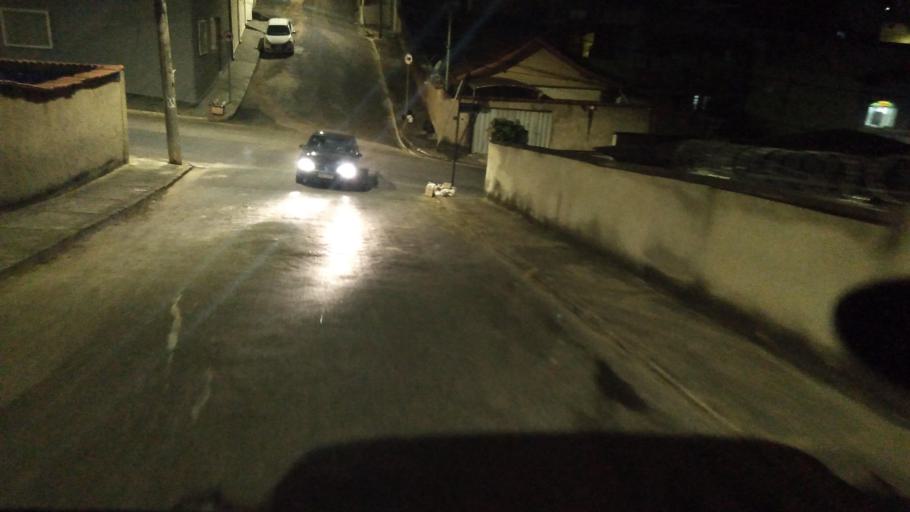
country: BR
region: Minas Gerais
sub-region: Belo Horizonte
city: Belo Horizonte
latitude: -19.8908
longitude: -43.9601
